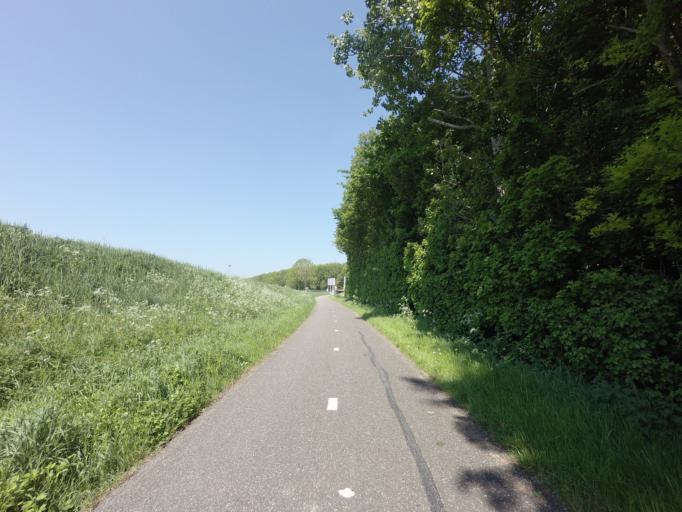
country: NL
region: Zeeland
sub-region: Gemeente Veere
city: Veere
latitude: 51.5242
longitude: 3.6826
